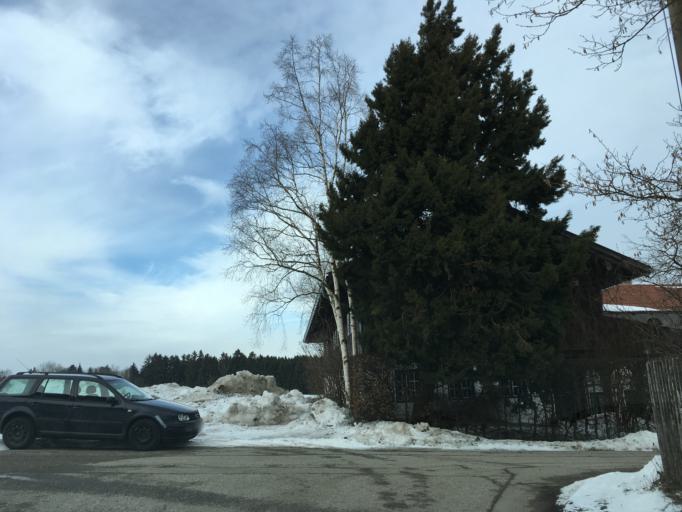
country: DE
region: Bavaria
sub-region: Upper Bavaria
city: Schnaitsee
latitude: 48.0824
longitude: 12.3761
